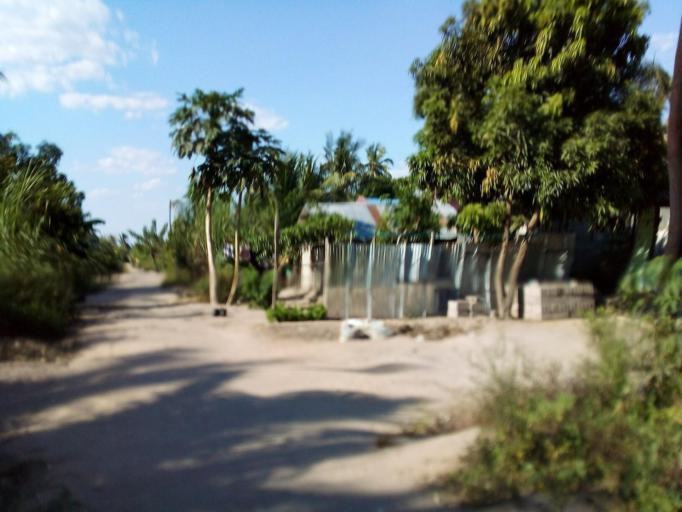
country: MZ
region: Zambezia
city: Quelimane
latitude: -17.5964
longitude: 36.8293
